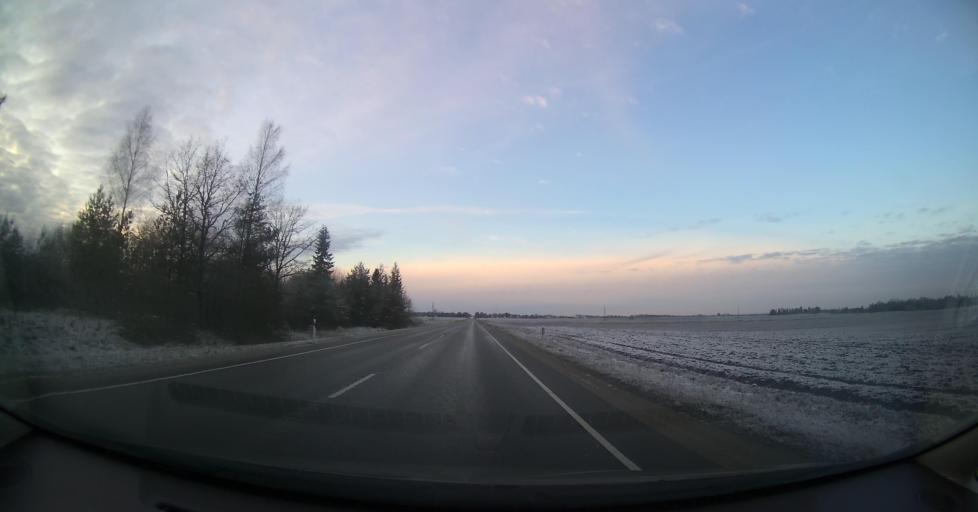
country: EE
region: Jogevamaa
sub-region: Poltsamaa linn
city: Poltsamaa
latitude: 58.6608
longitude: 26.0240
